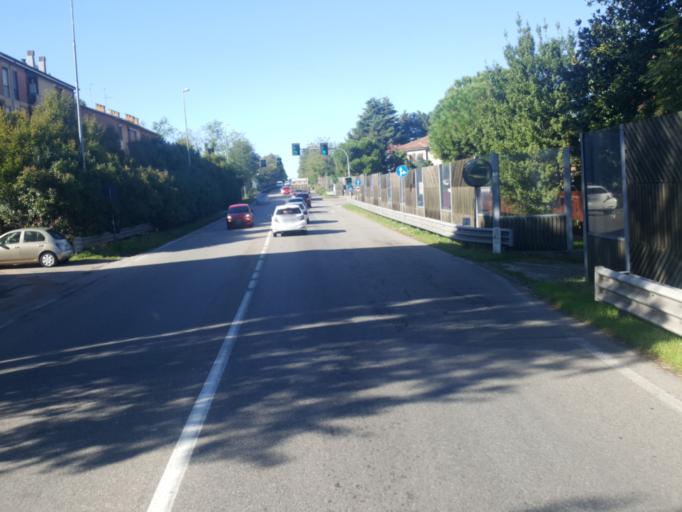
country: IT
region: Lombardy
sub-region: Citta metropolitana di Milano
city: Vittuone
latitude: 45.4854
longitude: 8.9446
